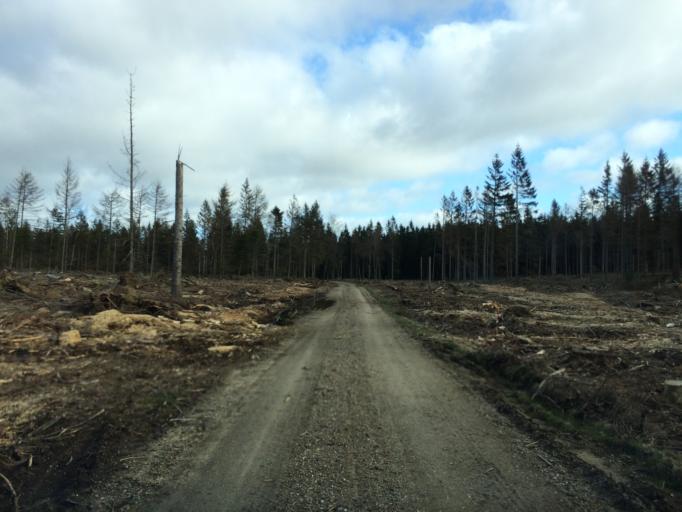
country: DK
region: Central Jutland
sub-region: Holstebro Kommune
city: Ulfborg
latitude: 56.2708
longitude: 8.4466
